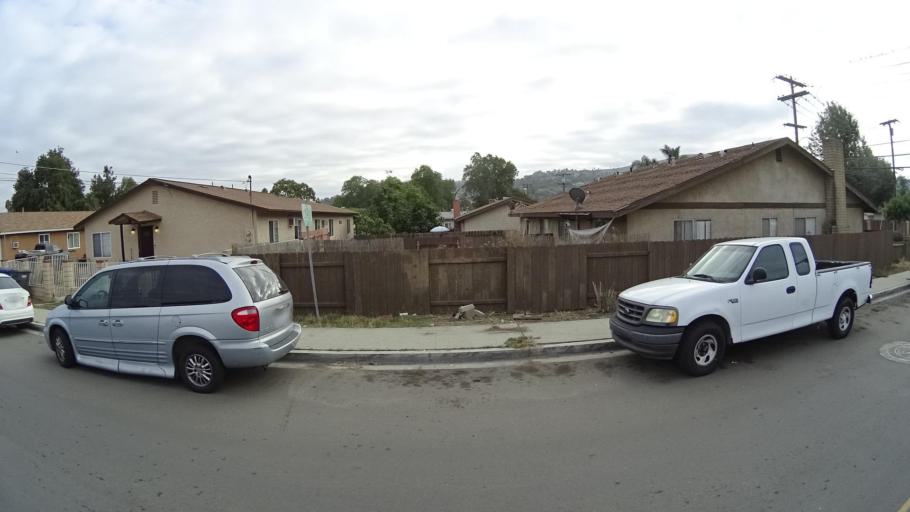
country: US
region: California
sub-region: San Diego County
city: Spring Valley
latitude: 32.7350
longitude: -117.0103
